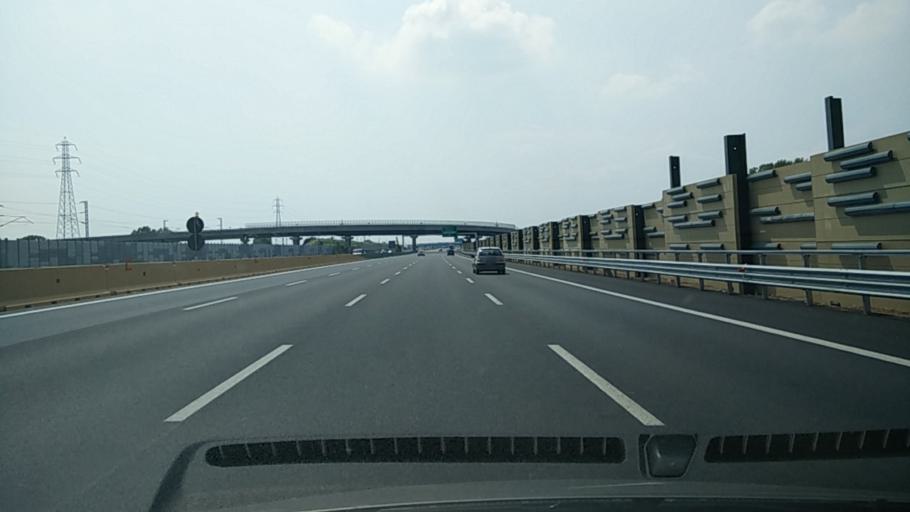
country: IT
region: Lombardy
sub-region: Citta metropolitana di Milano
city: Casone
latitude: 45.4935
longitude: 8.8830
